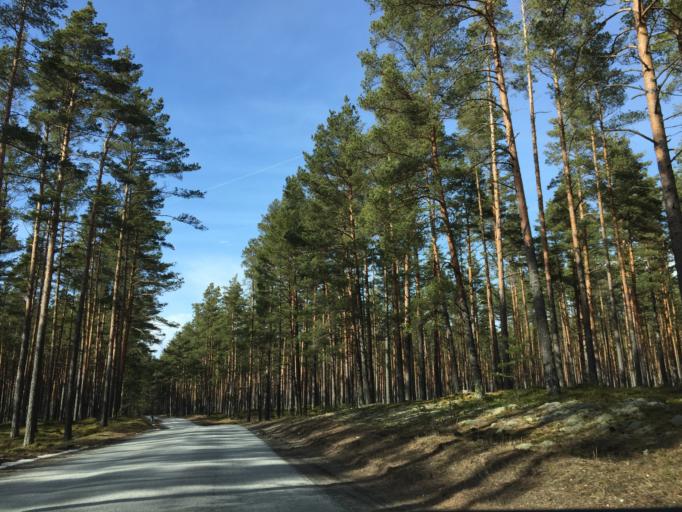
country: EE
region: Paernumaa
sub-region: Paernu linn
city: Parnu
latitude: 58.2382
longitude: 24.5259
